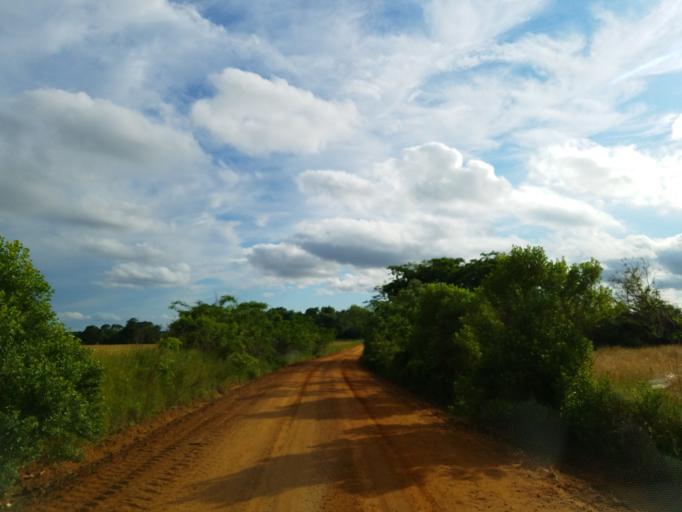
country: US
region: Georgia
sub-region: Dooly County
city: Vienna
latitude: 32.1430
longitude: -83.7840
